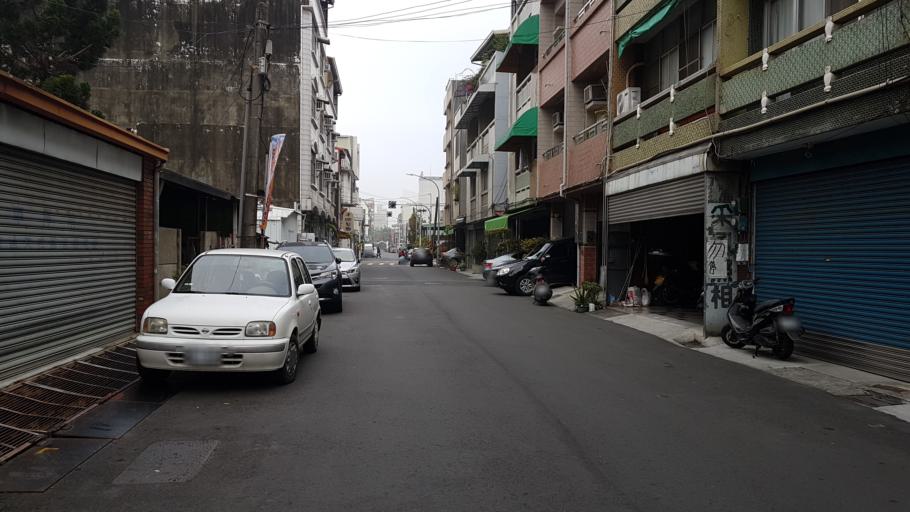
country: TW
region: Taiwan
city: Xinying
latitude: 23.3045
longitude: 120.3151
